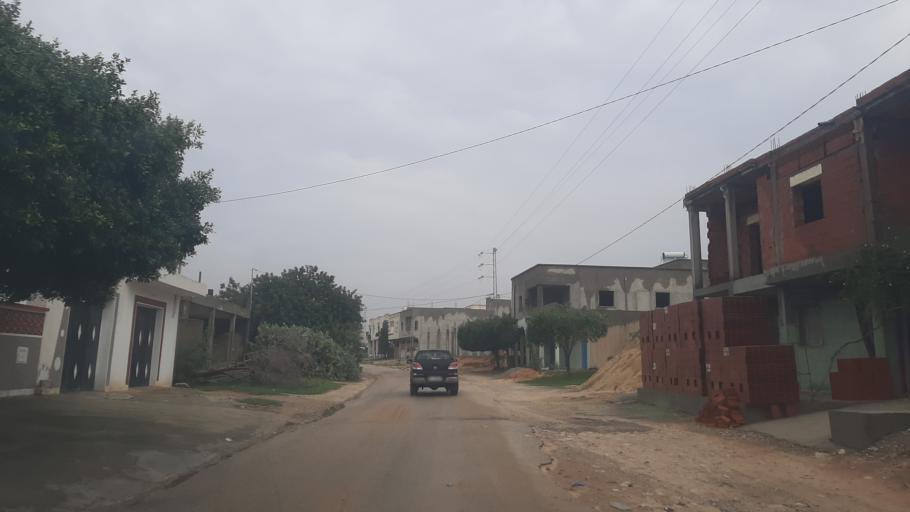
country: TN
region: Al Munastir
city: Sidi Bin Nur
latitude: 35.4769
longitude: 10.8748
